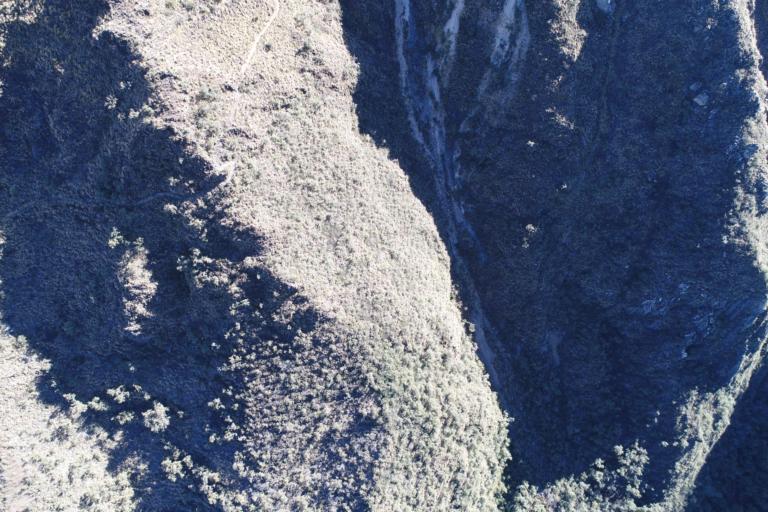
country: BO
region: La Paz
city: Viloco
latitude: -16.8202
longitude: -67.5454
